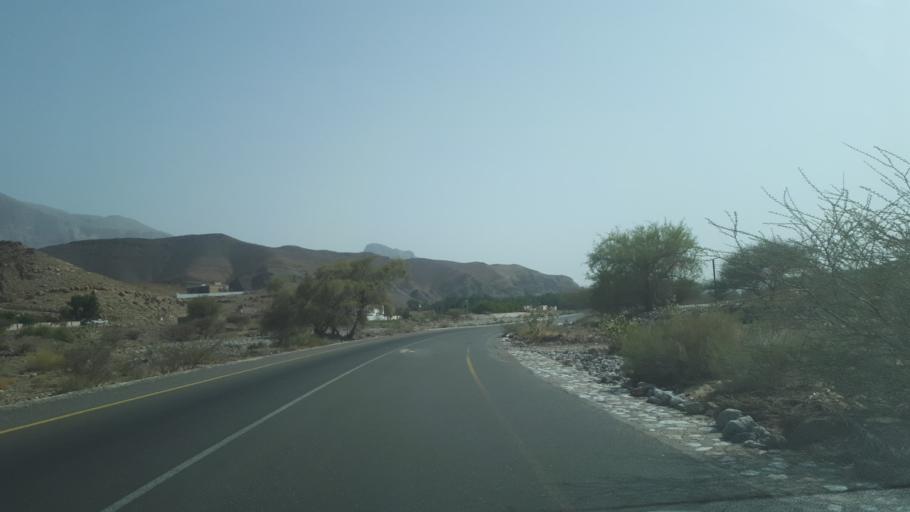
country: OM
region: Muhafazat ad Dakhiliyah
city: Bahla'
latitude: 23.2153
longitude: 56.9668
